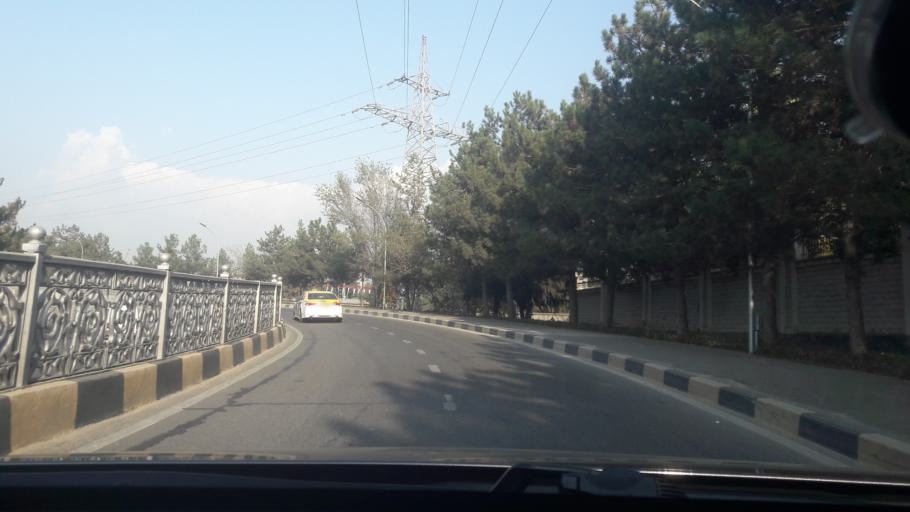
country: TJ
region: Dushanbe
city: Dushanbe
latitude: 38.5818
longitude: 68.7742
